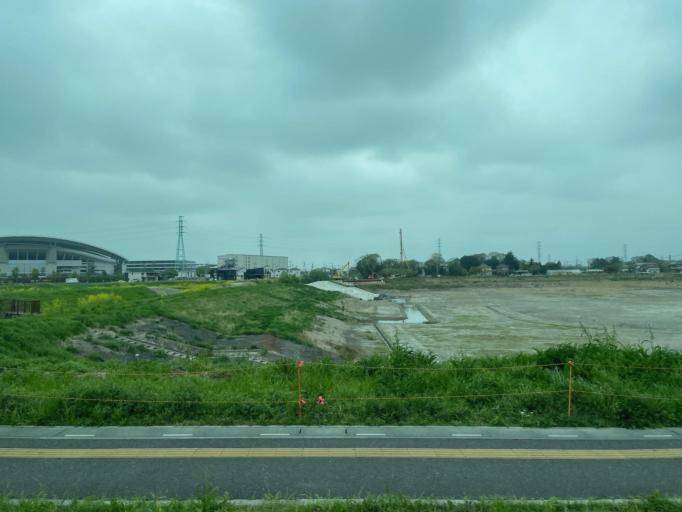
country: JP
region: Saitama
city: Koshigaya
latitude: 35.9029
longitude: 139.7263
